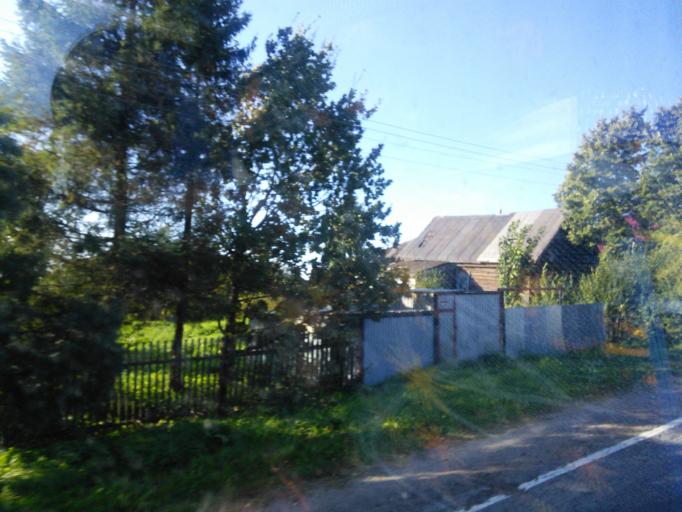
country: RU
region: Jaroslavl
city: Rybinsk
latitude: 58.2624
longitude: 38.8496
